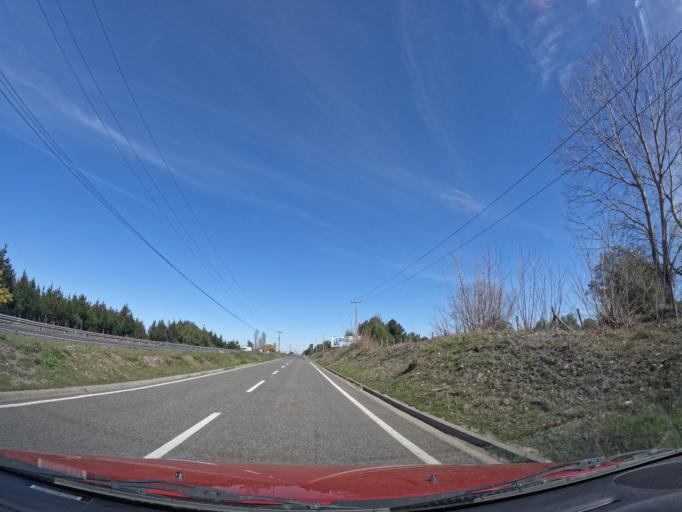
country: CL
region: Biobio
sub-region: Provincia de Biobio
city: Cabrero
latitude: -37.0188
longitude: -72.3664
